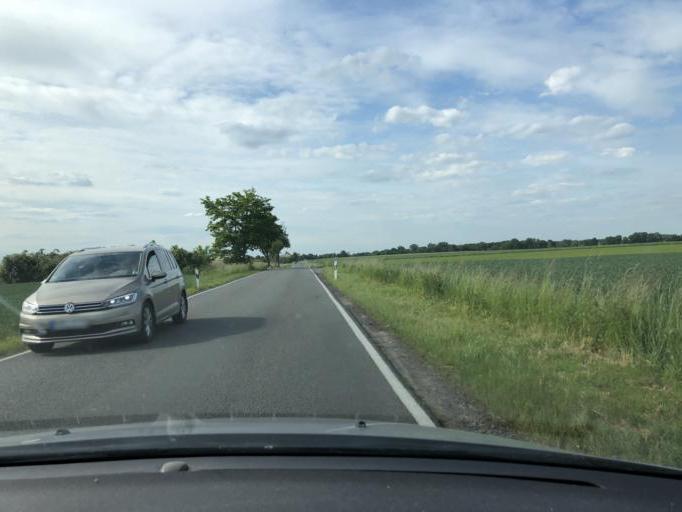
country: DE
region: Saxony
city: Nerchau
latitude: 51.2803
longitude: 12.7800
